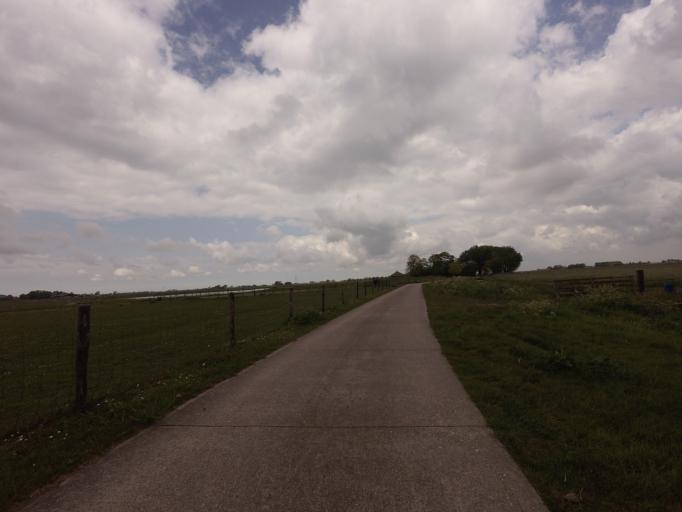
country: NL
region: Friesland
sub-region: Gemeente Littenseradiel
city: Wommels
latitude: 53.1106
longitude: 5.6004
